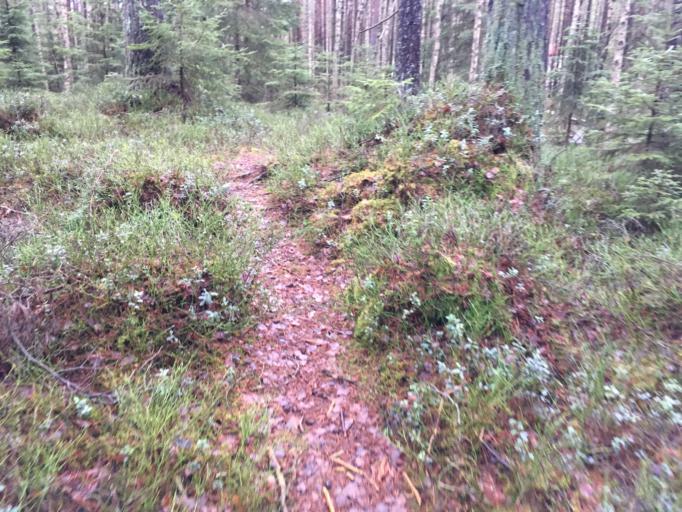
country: SE
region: Vaestra Goetaland
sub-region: Alingsas Kommun
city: Alingsas
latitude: 57.9018
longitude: 12.6255
